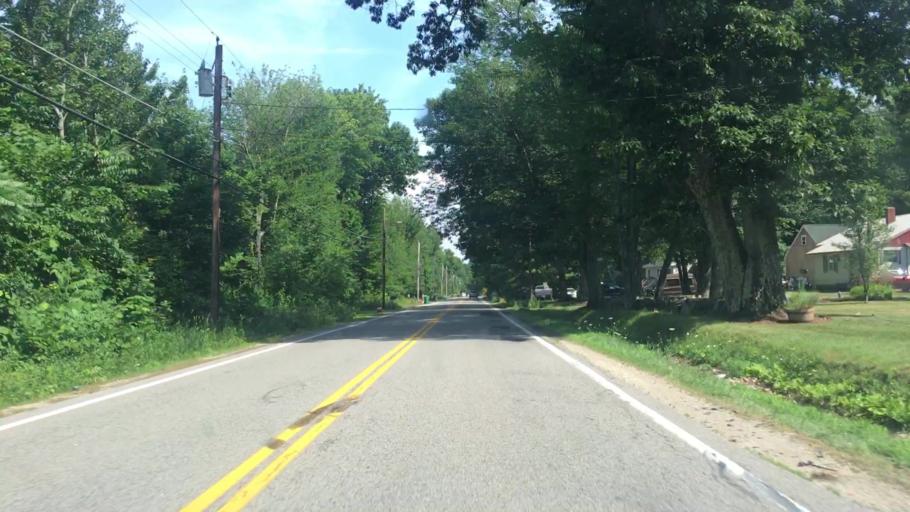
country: US
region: New Hampshire
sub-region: Strafford County
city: Rochester
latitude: 43.3161
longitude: -70.9373
